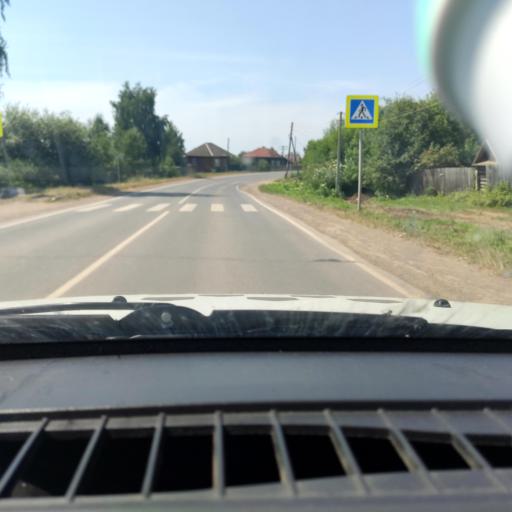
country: RU
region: Perm
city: Okhansk
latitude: 57.7149
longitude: 55.3624
